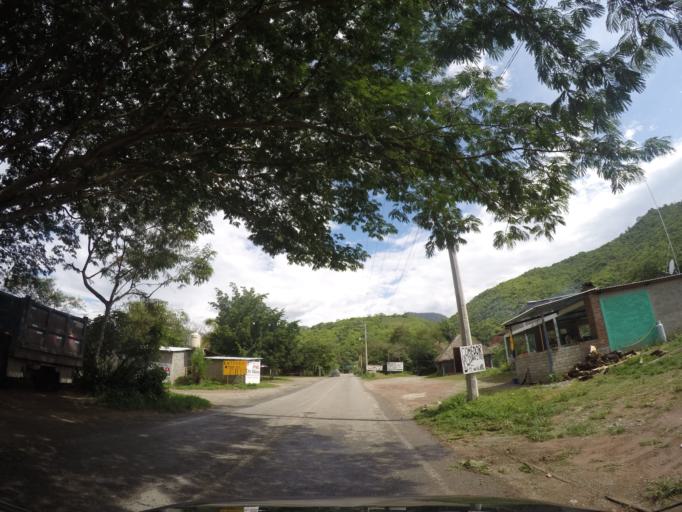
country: MX
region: Oaxaca
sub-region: San Jeronimo Coatlan
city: San Cristobal Honduras
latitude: 16.3494
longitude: -97.0949
